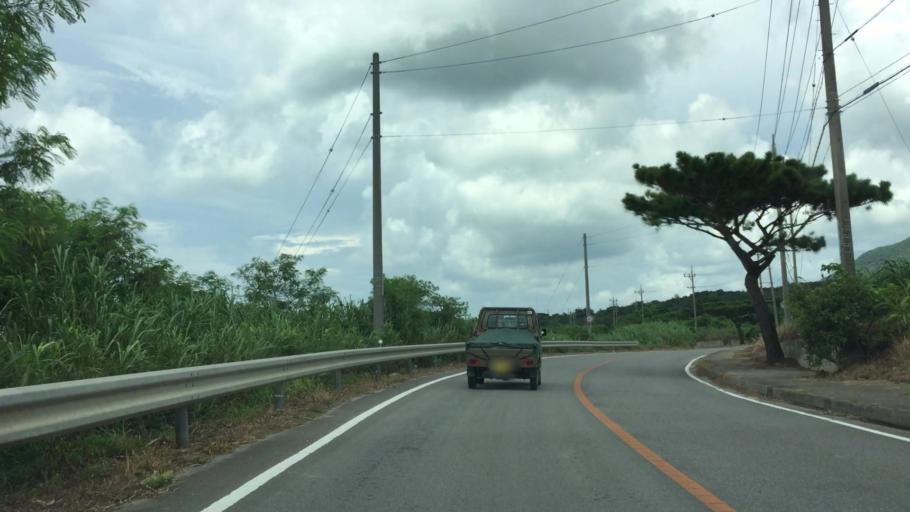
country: JP
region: Okinawa
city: Ishigaki
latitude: 24.3989
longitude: 124.1519
